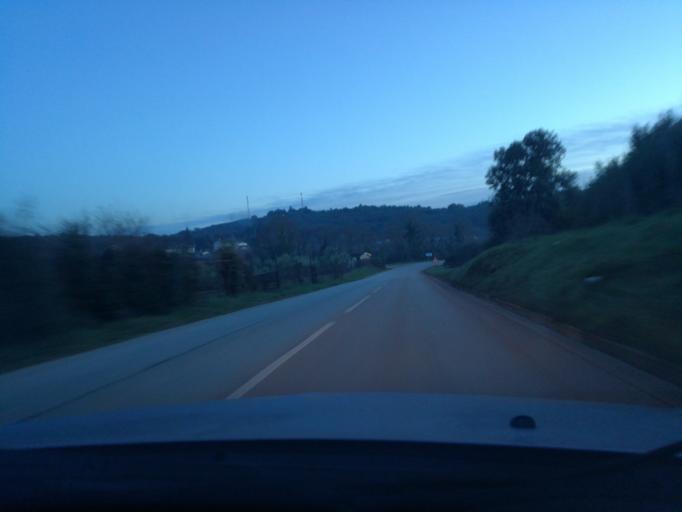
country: HR
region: Istarska
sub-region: Grad Rovinj
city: Rovinj
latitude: 45.1018
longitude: 13.6439
